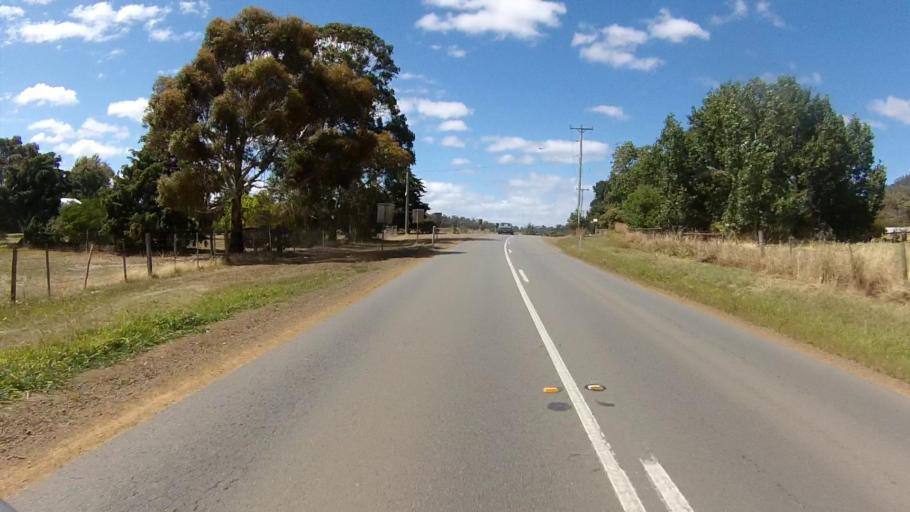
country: AU
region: Tasmania
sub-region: Clarence
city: Cambridge
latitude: -42.8132
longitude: 147.4321
